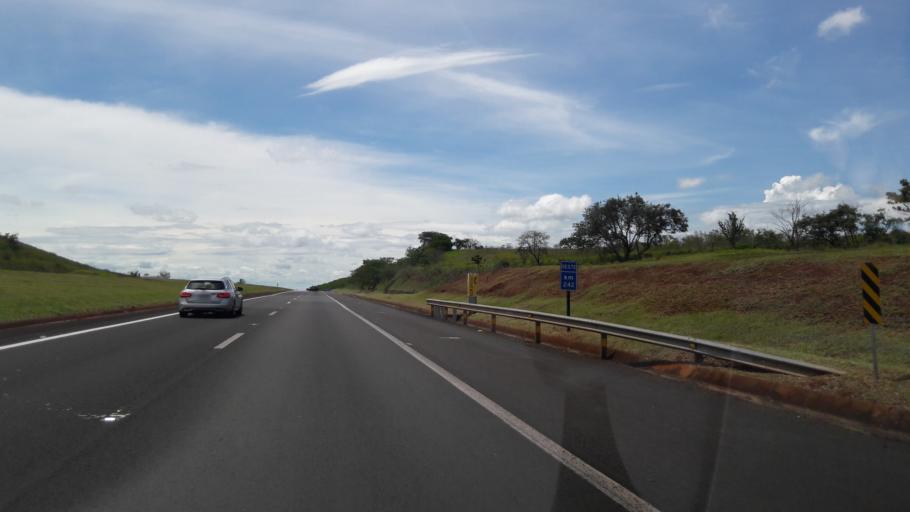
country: BR
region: Sao Paulo
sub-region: Avare
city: Avare
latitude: -22.9600
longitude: -48.8132
